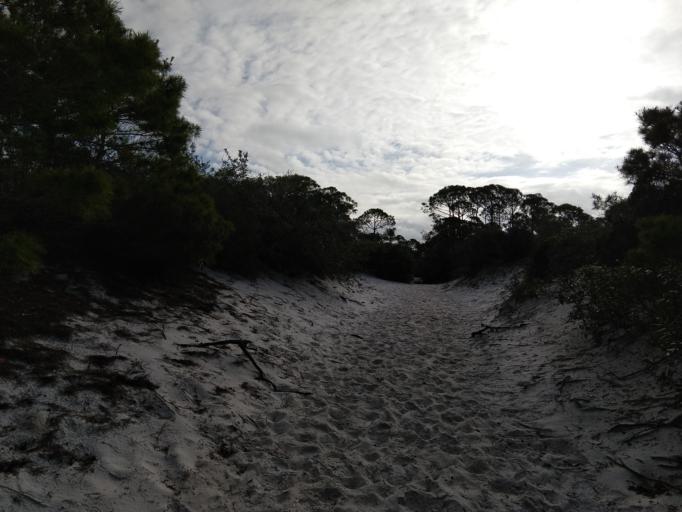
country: US
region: Florida
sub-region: Gulf County
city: Port Saint Joe
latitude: 29.7891
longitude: -85.4088
